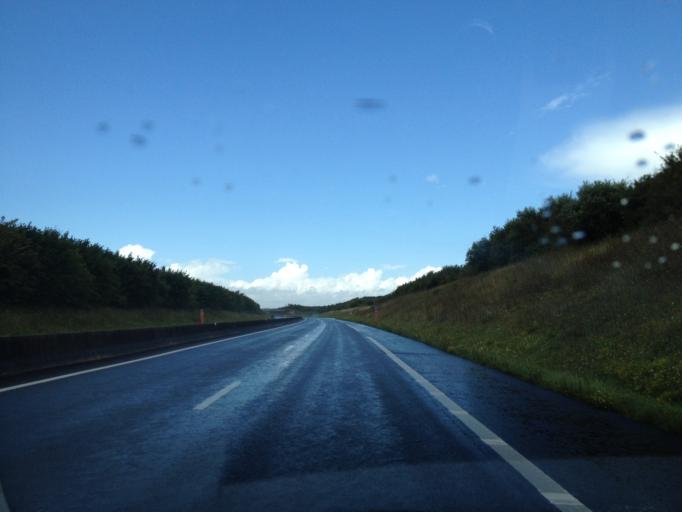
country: FR
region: Nord-Pas-de-Calais
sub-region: Departement du Pas-de-Calais
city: Verton
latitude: 50.3770
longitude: 1.6973
